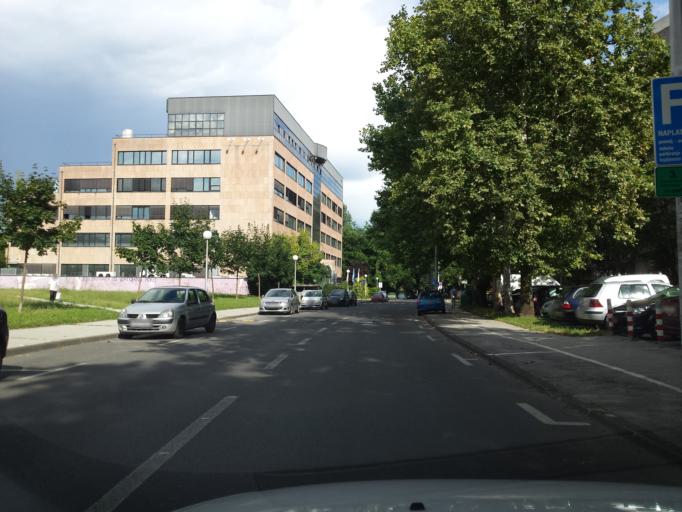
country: HR
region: Grad Zagreb
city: Novi Zagreb
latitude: 45.7944
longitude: 15.9978
